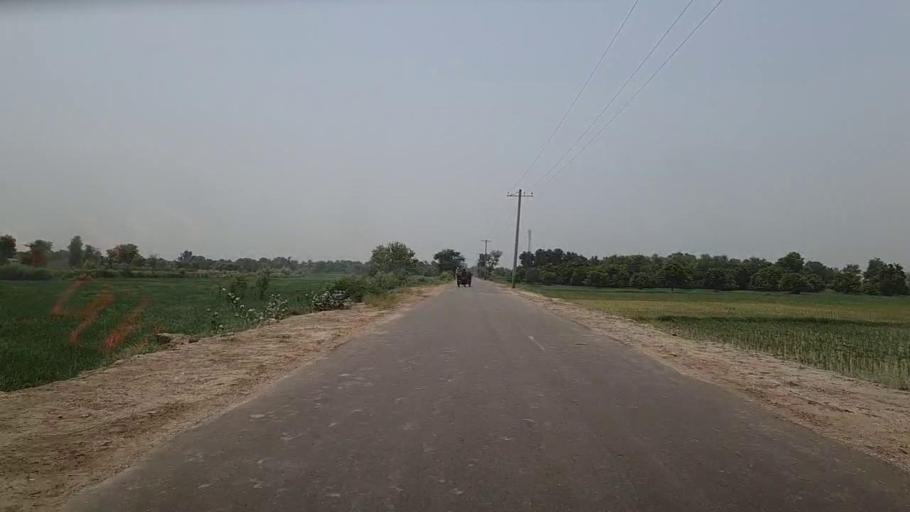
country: PK
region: Sindh
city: Sita Road
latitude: 27.0459
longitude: 67.9009
